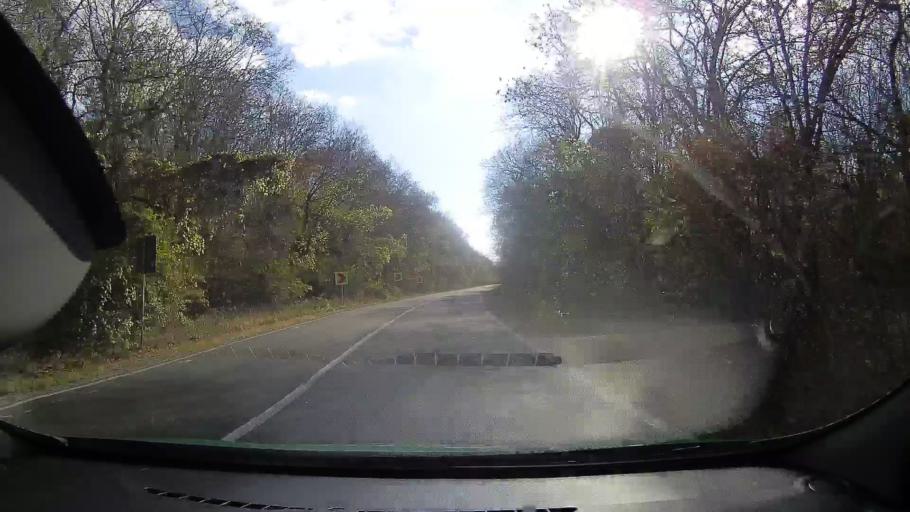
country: RO
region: Tulcea
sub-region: Oras Babadag
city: Babadag
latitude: 44.8497
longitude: 28.6976
